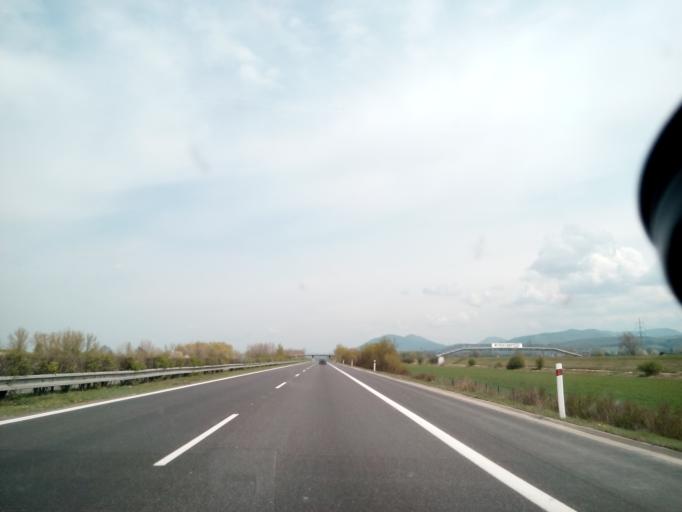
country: SK
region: Nitriansky
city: Dubnica nad Vahom
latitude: 48.9756
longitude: 18.1704
